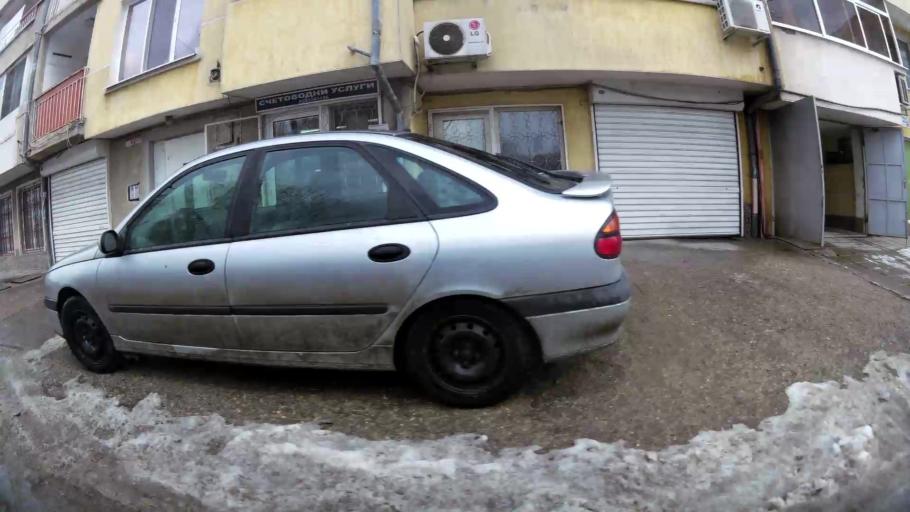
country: BG
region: Sofia-Capital
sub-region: Stolichna Obshtina
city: Sofia
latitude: 42.7076
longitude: 23.3701
